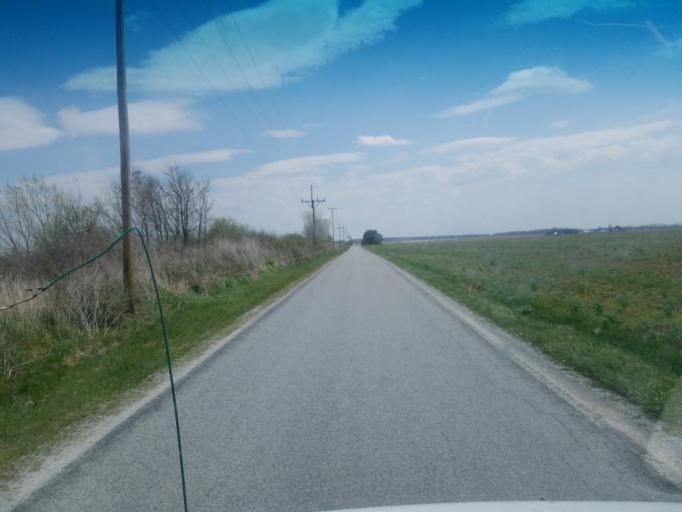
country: US
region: Ohio
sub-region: Hardin County
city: Forest
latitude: 40.7599
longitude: -83.5311
